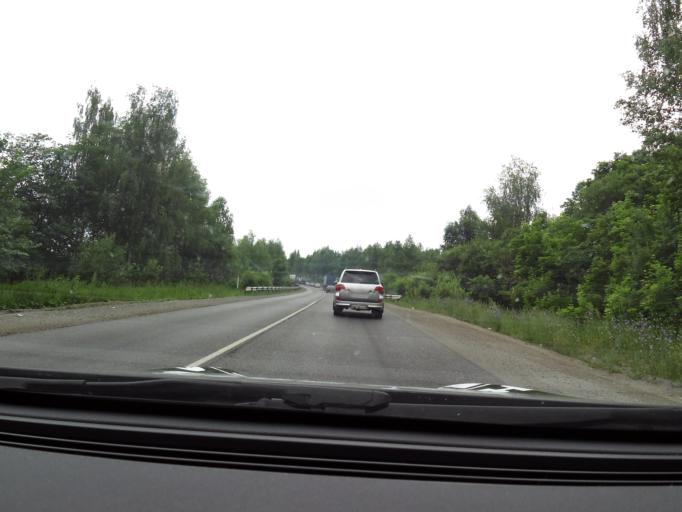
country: RU
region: Chelyabinsk
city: Sim
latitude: 54.9996
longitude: 57.6202
